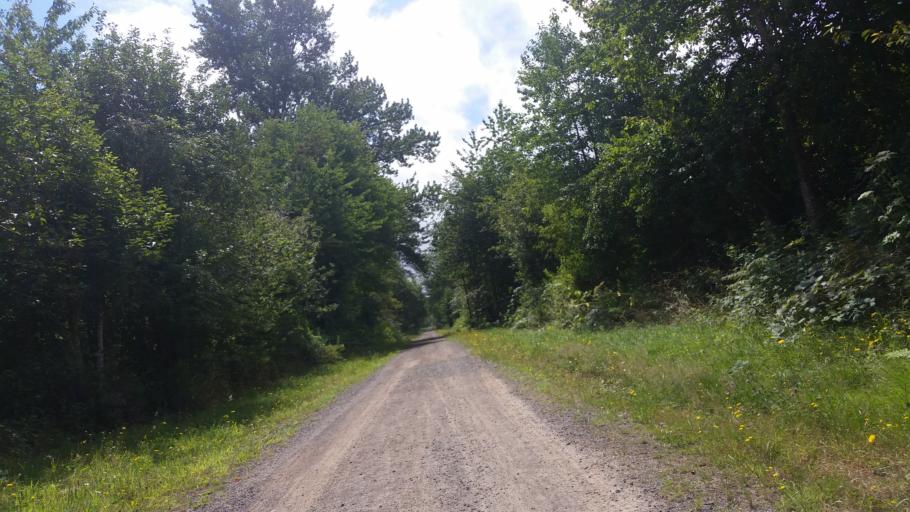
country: US
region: Washington
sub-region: King County
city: North Bend
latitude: 47.5105
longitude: -121.7927
